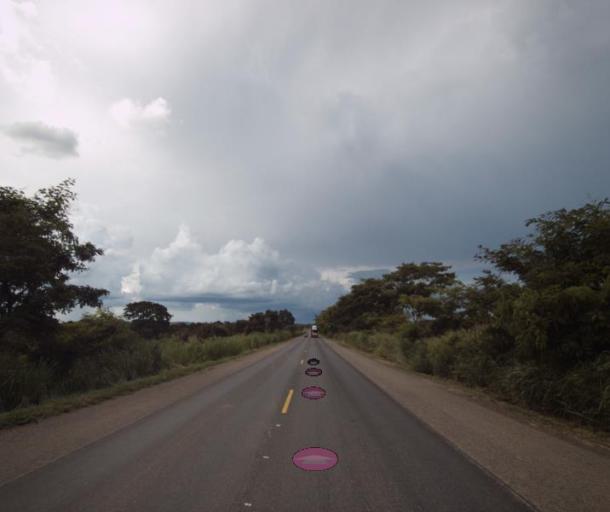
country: BR
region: Goias
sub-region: Ceres
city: Ceres
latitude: -15.2193
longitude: -49.5511
